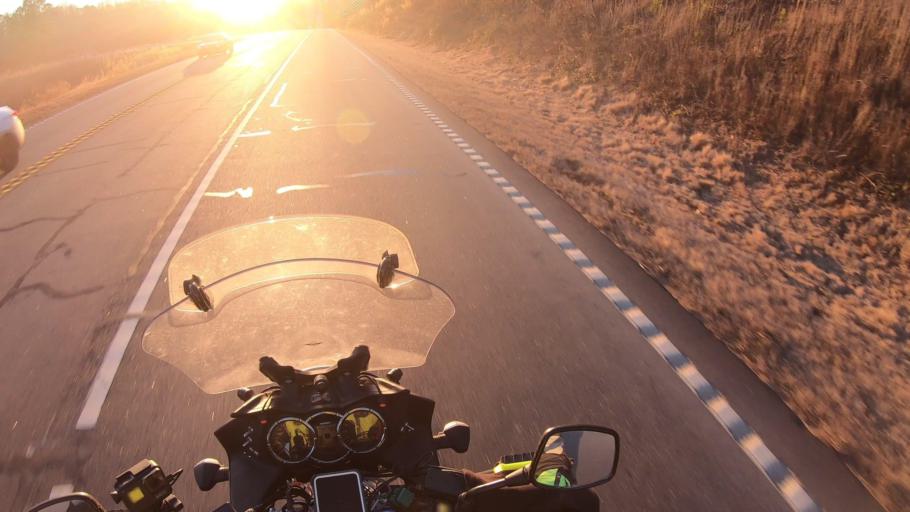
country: US
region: Georgia
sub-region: Forsyth County
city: Cumming
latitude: 34.3026
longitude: -84.2253
